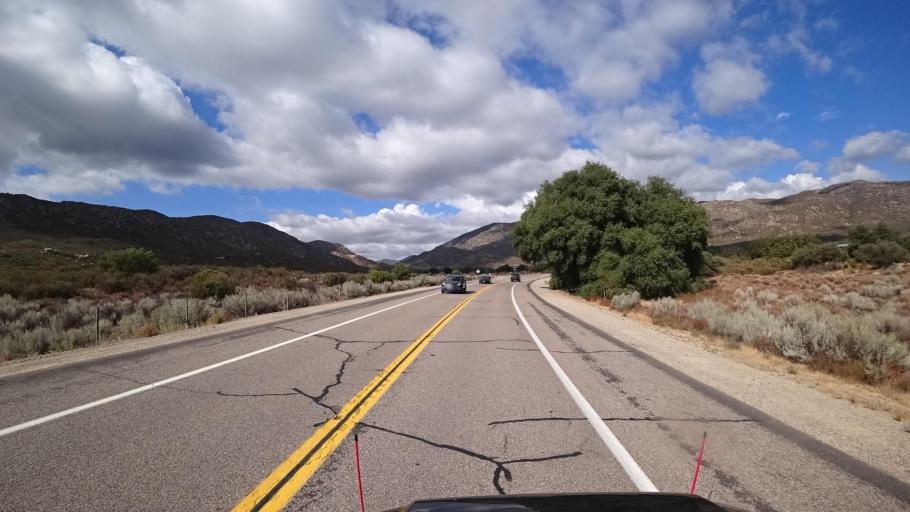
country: US
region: California
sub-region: San Diego County
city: Pine Valley
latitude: 32.7558
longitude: -116.4933
